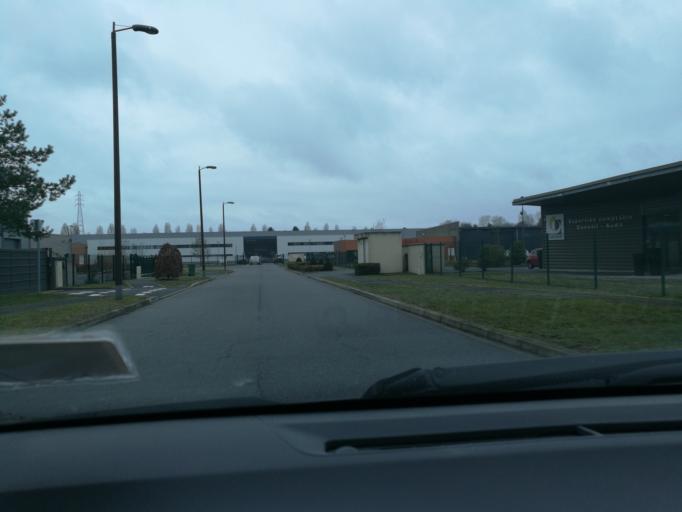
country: FR
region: Centre
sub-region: Departement du Loiret
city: Fleury-les-Aubrais
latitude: 47.9474
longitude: 1.9276
